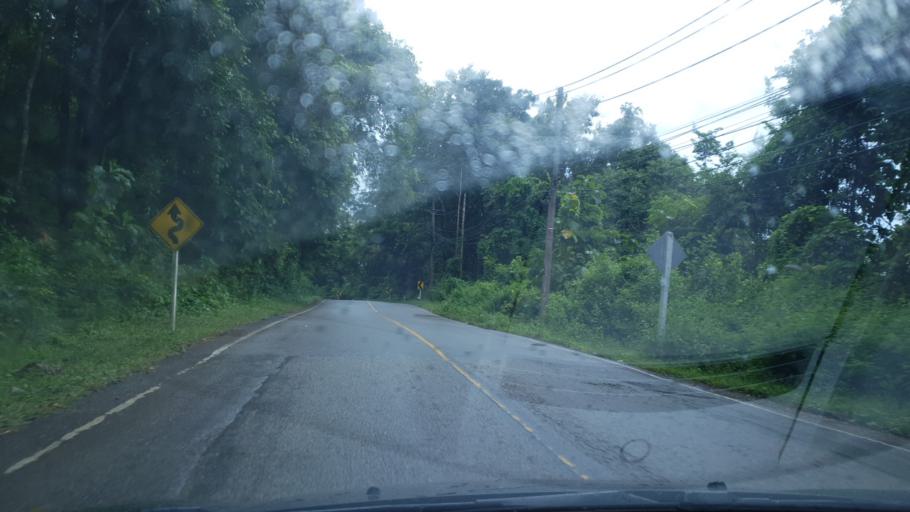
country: TH
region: Mae Hong Son
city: Pa Pae
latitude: 18.2799
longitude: 97.9386
